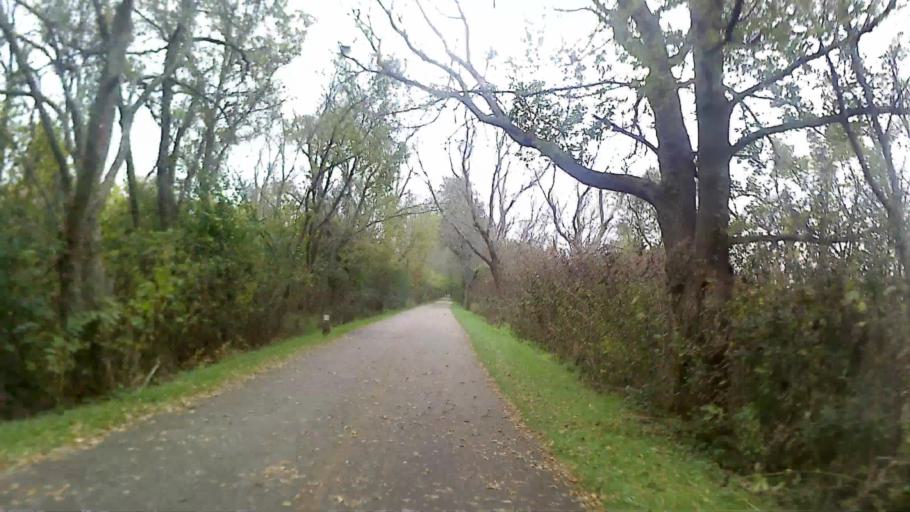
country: US
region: Illinois
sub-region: Kane County
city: Sugar Grove
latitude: 41.7713
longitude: -88.4082
